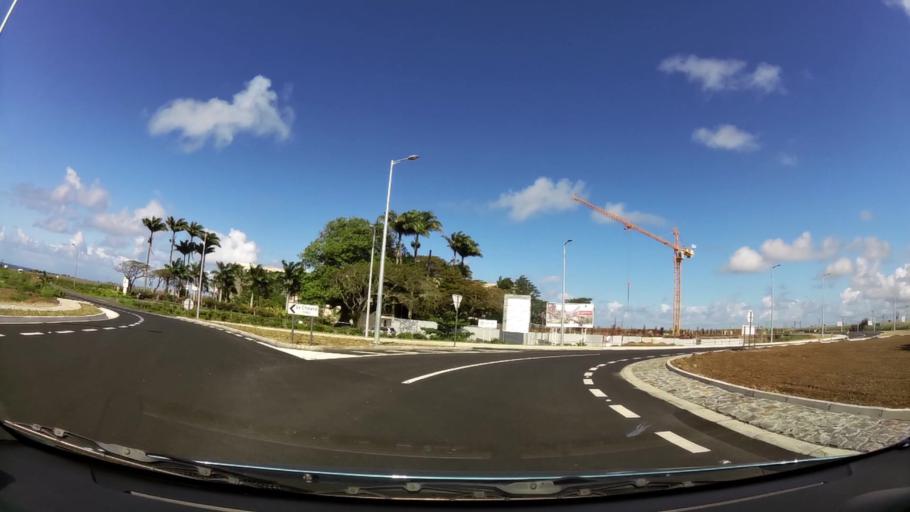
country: MU
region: Grand Port
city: Plaine Magnien
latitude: -20.4390
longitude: 57.6713
